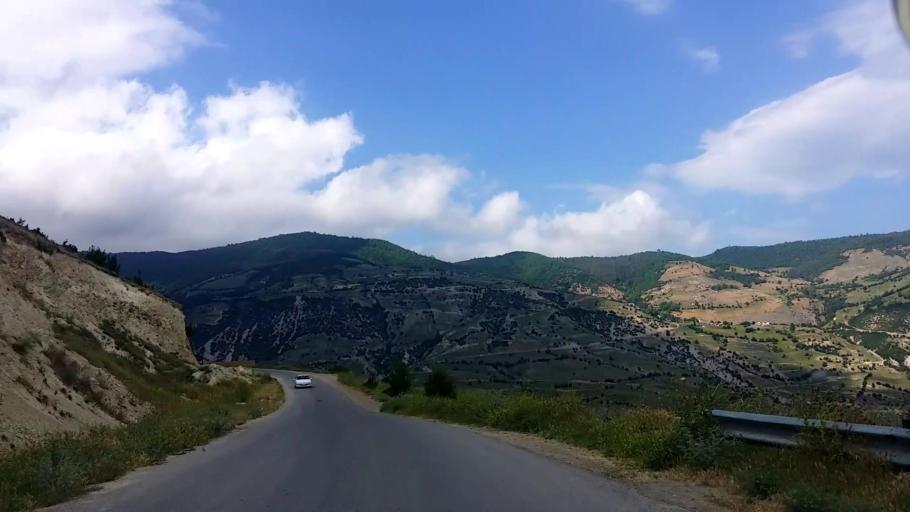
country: IR
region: Mazandaran
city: Chalus
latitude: 36.5386
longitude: 51.2727
